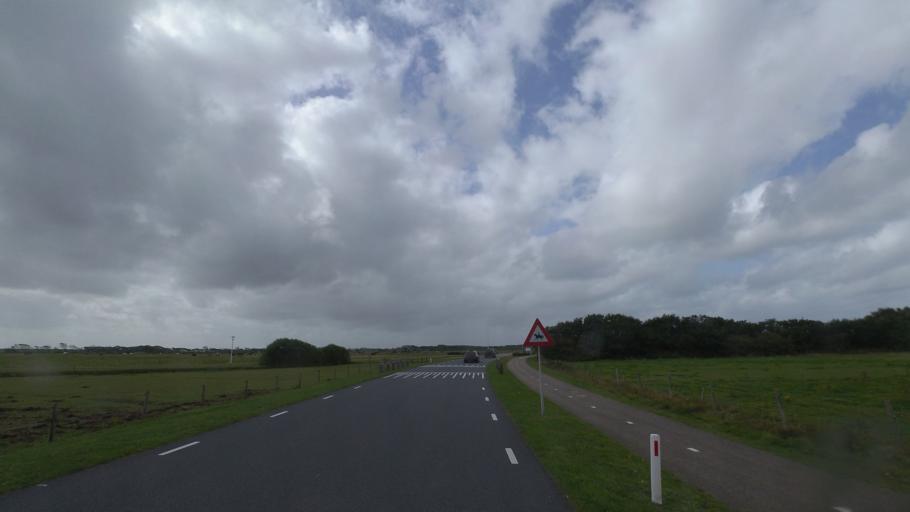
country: NL
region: Friesland
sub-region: Gemeente Ameland
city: Hollum
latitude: 53.4462
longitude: 5.6828
